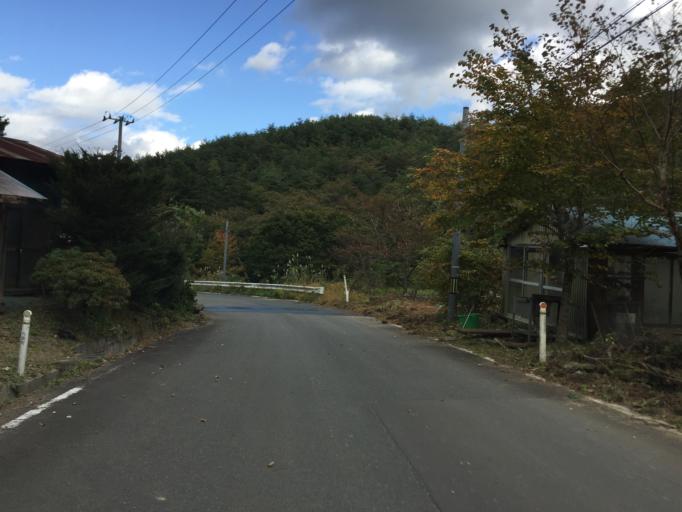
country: JP
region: Miyagi
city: Marumori
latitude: 37.8174
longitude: 140.7920
